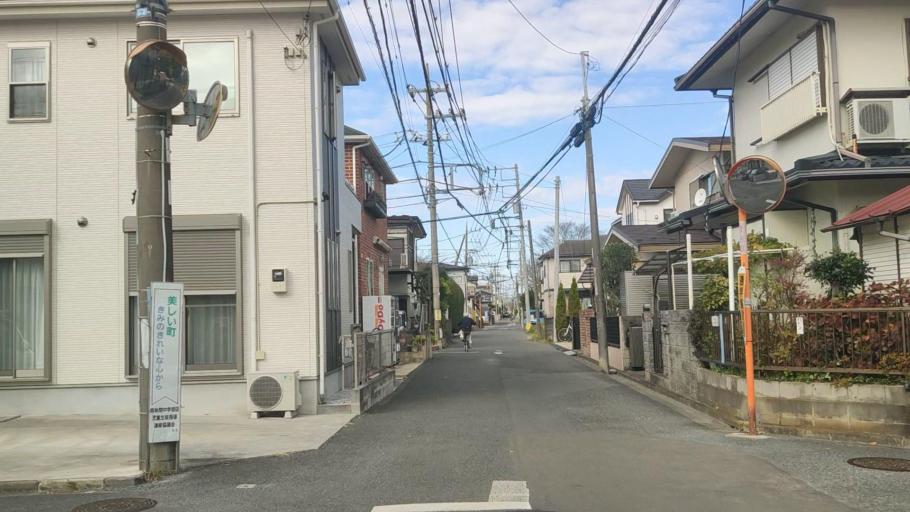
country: JP
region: Kanagawa
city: Minami-rinkan
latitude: 35.4868
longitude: 139.4388
